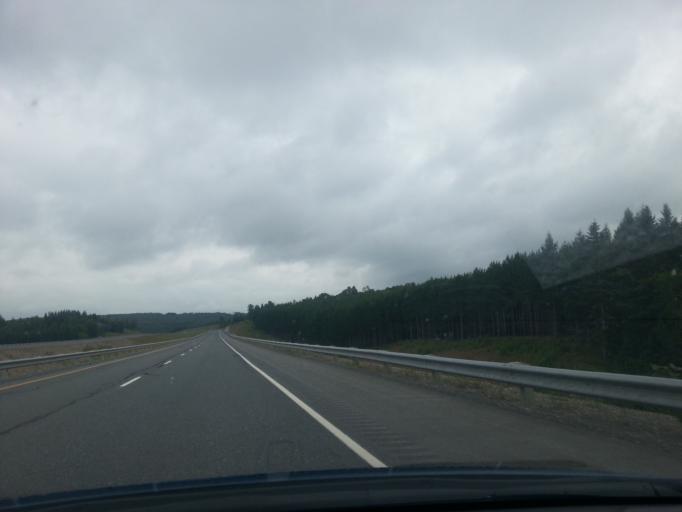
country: US
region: Maine
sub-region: Aroostook County
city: Easton
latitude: 46.5807
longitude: -67.7452
